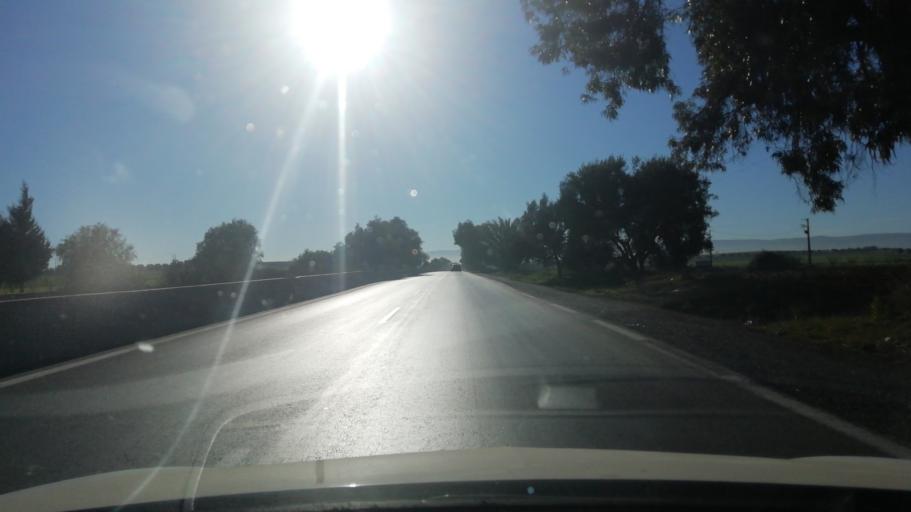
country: DZ
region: Tlemcen
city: Hennaya
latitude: 35.0073
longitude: -1.3886
